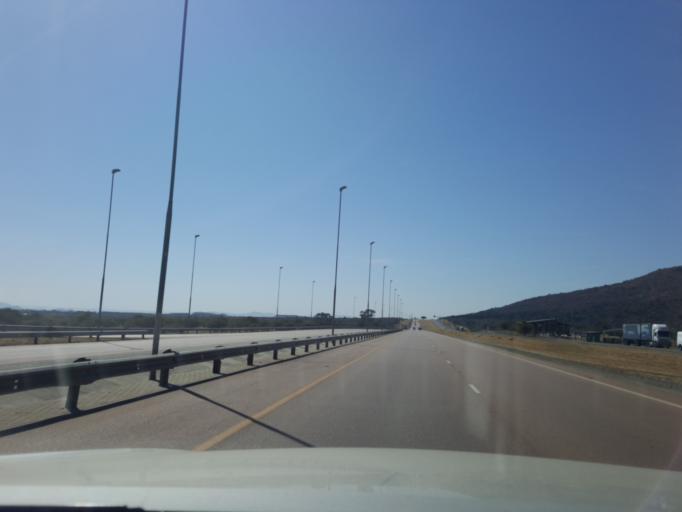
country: ZA
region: North-West
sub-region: Bojanala Platinum District Municipality
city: Brits
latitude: -25.7194
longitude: 27.6852
